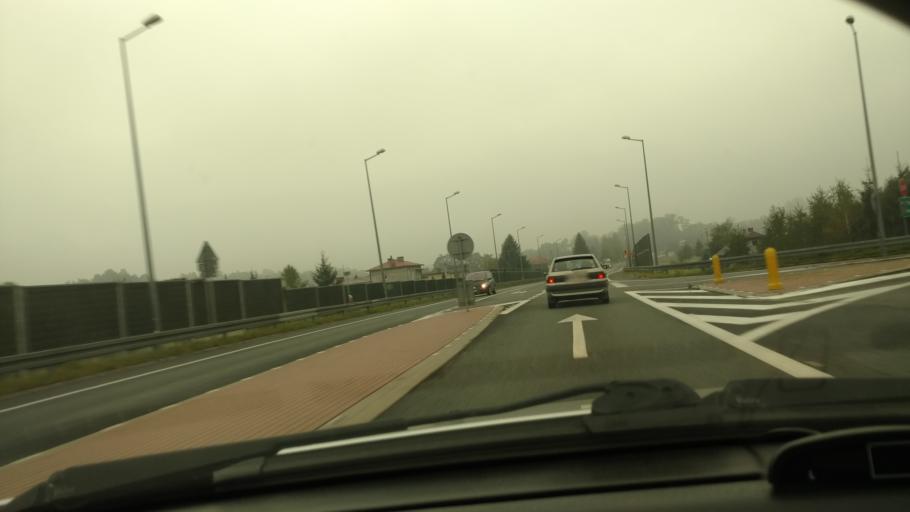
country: PL
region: Lesser Poland Voivodeship
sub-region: Powiat gorlicki
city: Biecz
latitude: 49.7080
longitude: 21.2398
